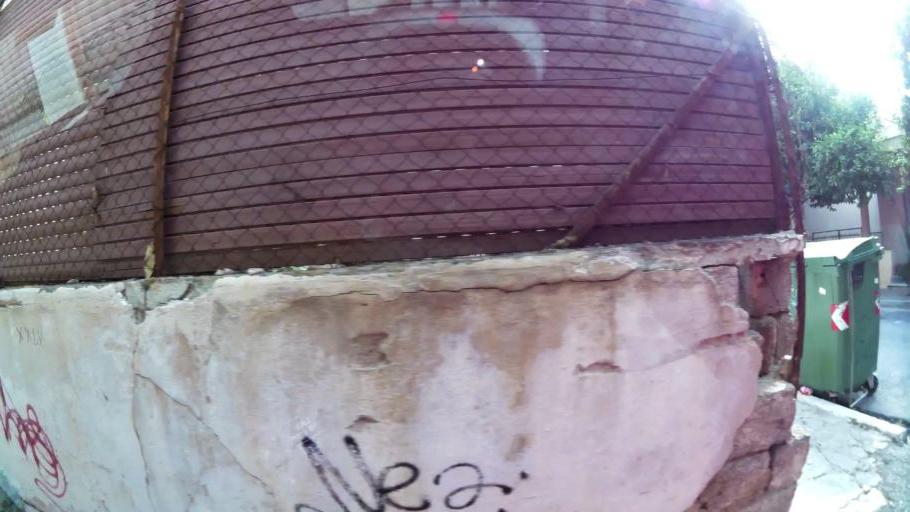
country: GR
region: Attica
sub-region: Nomarchia Athinas
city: Peristeri
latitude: 38.0264
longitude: 23.6843
